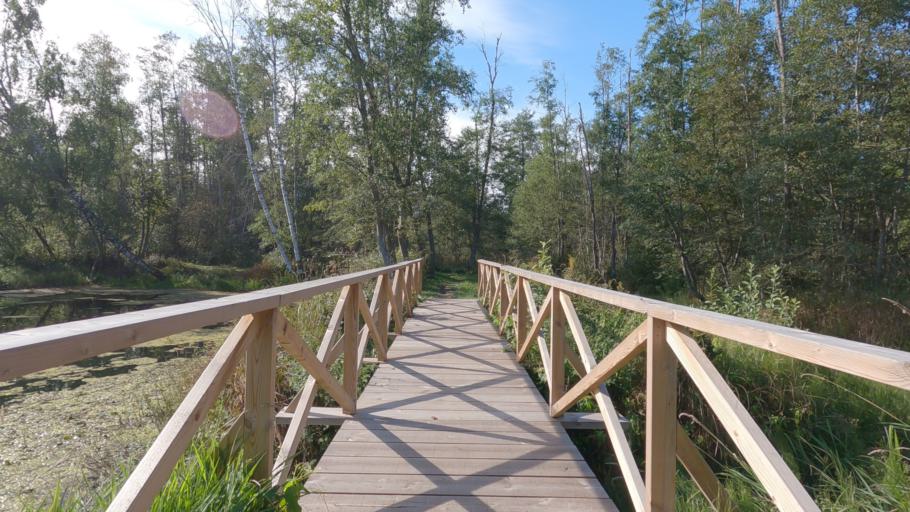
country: EE
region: Raplamaa
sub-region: Rapla vald
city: Rapla
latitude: 58.9998
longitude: 24.8192
